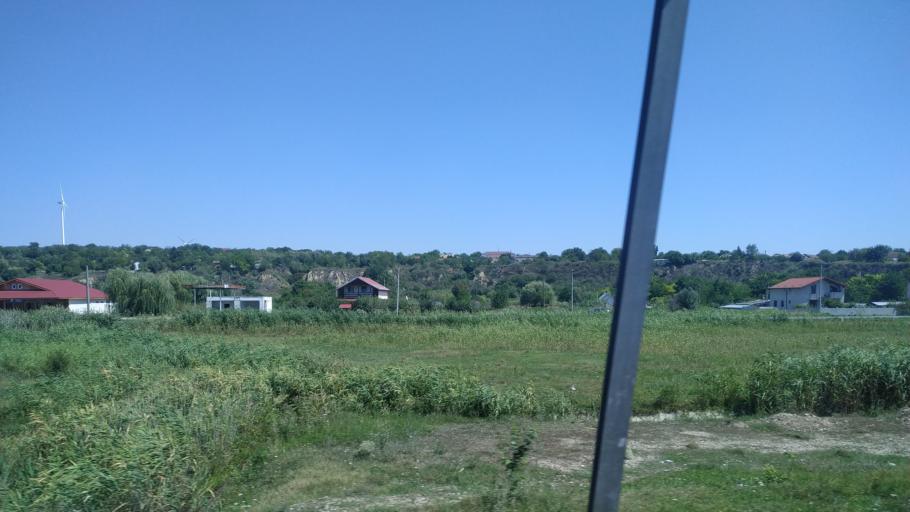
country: RO
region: Constanta
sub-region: Comuna Saligny
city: Saligny
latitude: 44.2804
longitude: 28.0825
